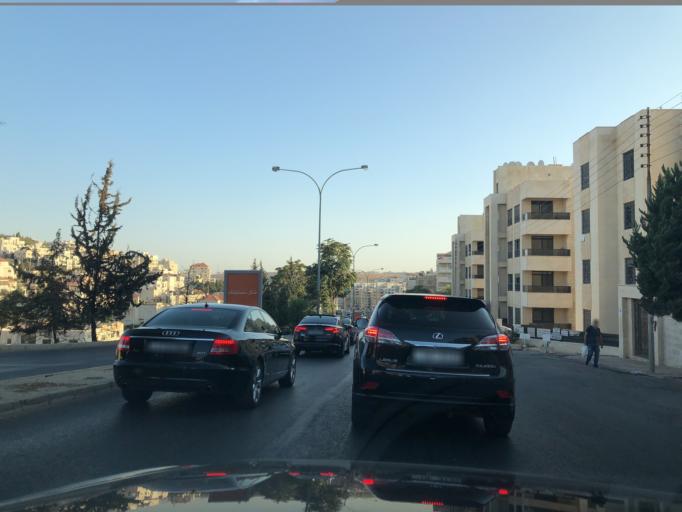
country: JO
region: Amman
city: Wadi as Sir
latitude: 31.9444
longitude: 35.8700
